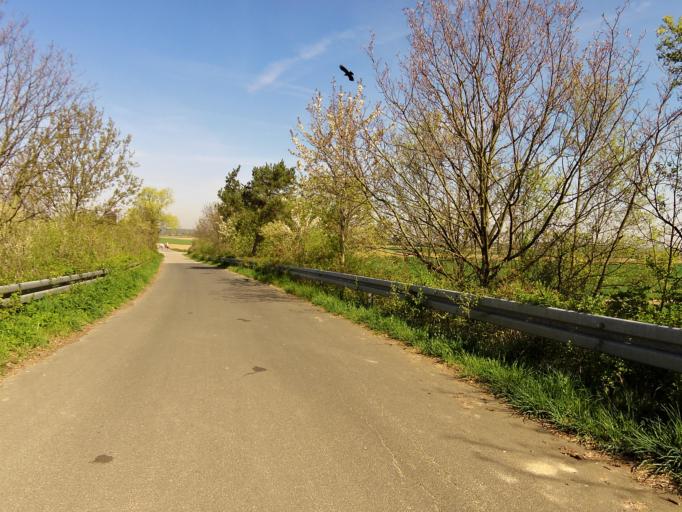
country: DE
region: North Rhine-Westphalia
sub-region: Regierungsbezirk Koln
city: Rheinbach
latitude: 50.6350
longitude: 6.9404
